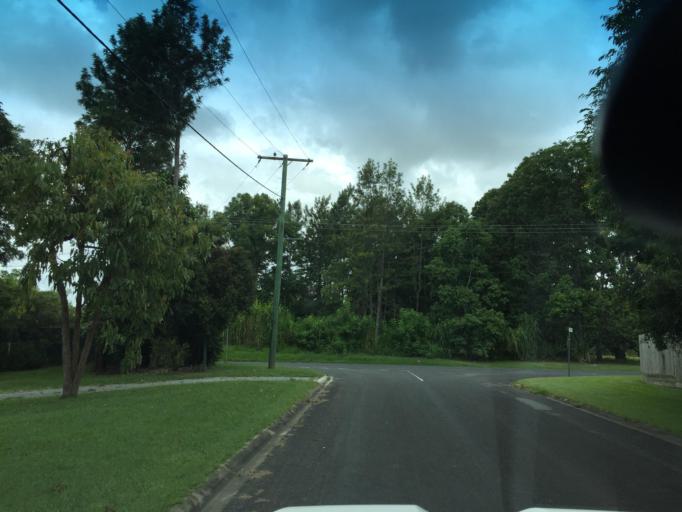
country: AU
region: Queensland
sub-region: Moreton Bay
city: Caboolture
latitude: -27.0442
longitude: 152.9229
